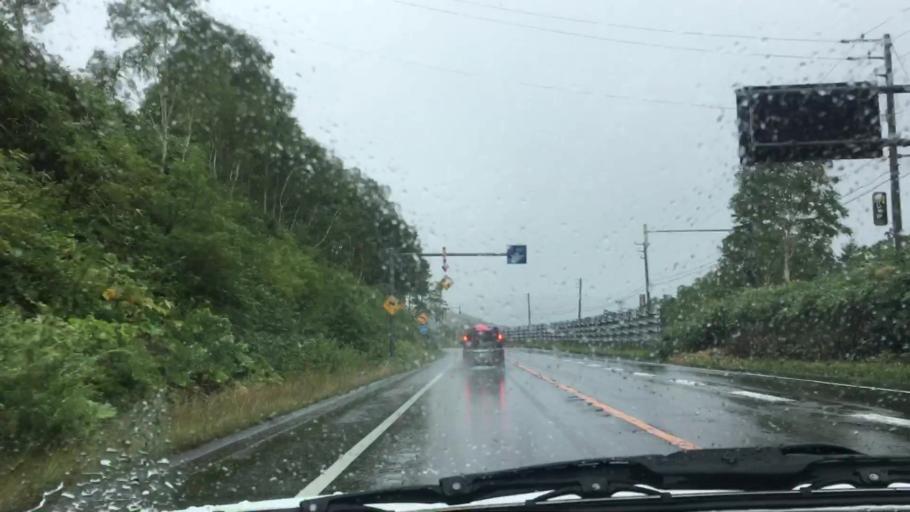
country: JP
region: Hokkaido
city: Sapporo
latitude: 42.8552
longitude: 141.0942
